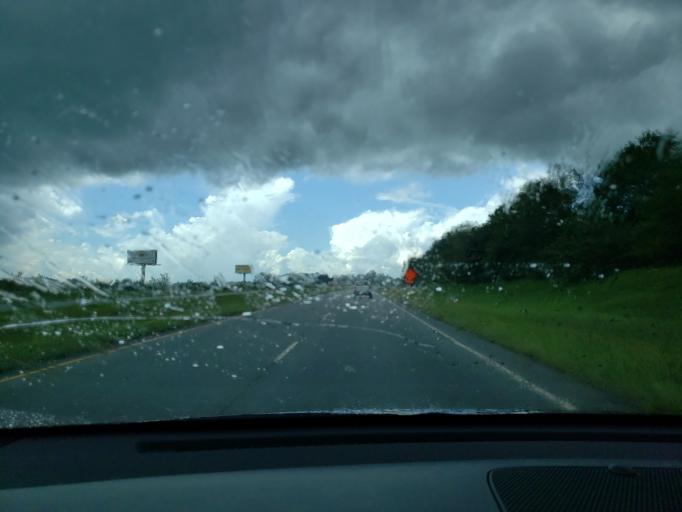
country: US
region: North Carolina
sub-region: Bladen County
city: Elizabethtown
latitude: 34.6045
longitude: -78.6241
